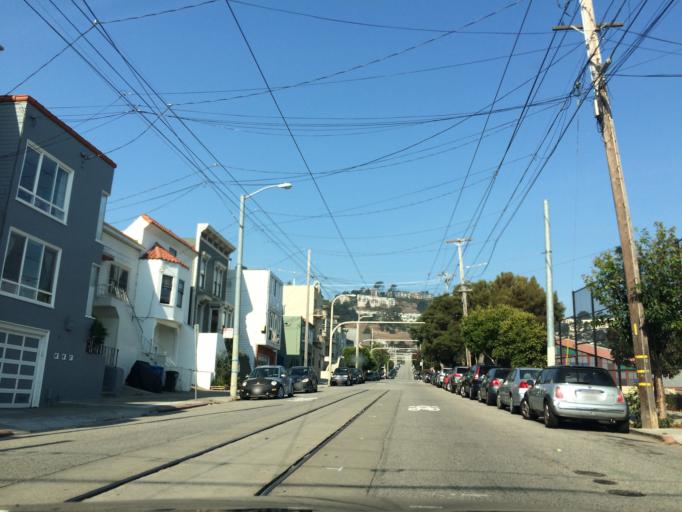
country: US
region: California
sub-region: San Francisco County
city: San Francisco
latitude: 37.7421
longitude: -122.4269
